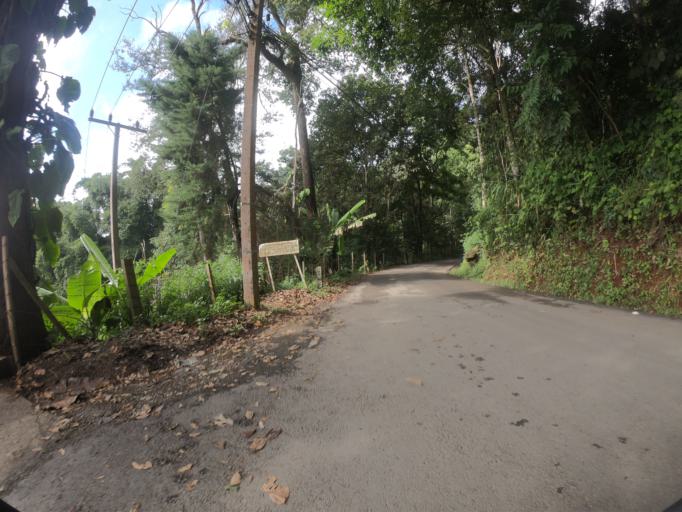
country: TH
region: Chiang Mai
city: Chiang Mai
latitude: 18.8123
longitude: 98.8844
